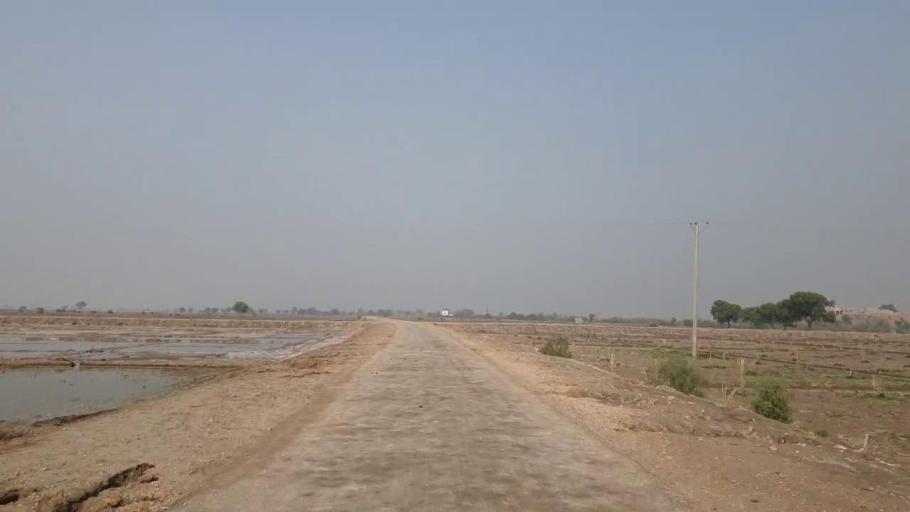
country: PK
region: Sindh
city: Bhan
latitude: 26.4841
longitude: 67.7010
